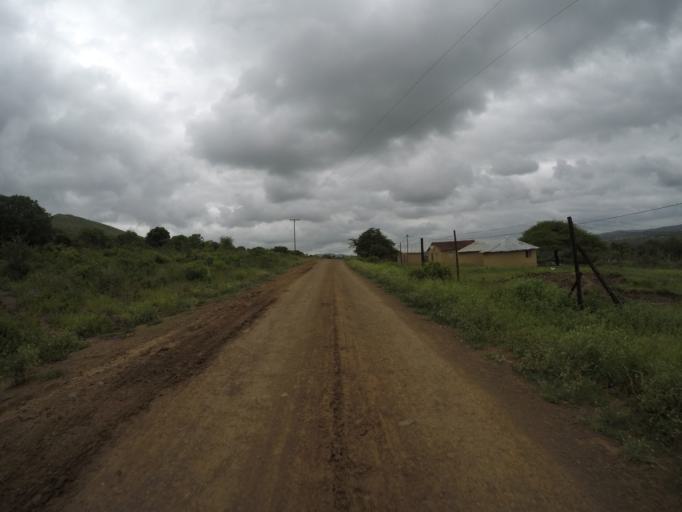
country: ZA
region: KwaZulu-Natal
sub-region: uThungulu District Municipality
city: Empangeni
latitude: -28.5715
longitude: 31.8731
